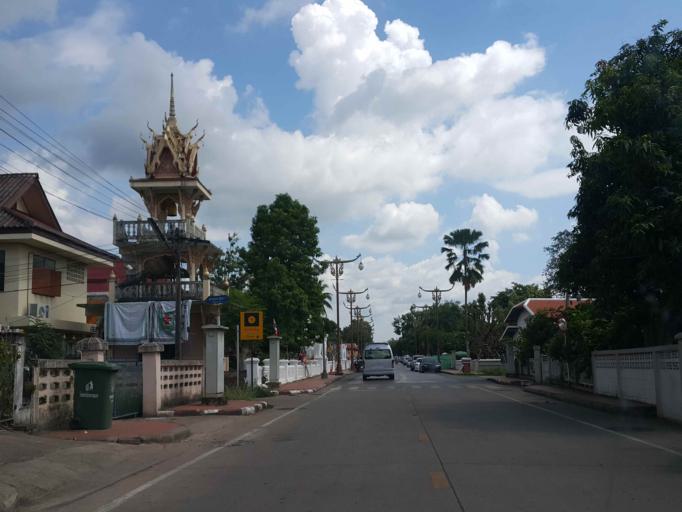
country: TH
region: Nan
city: Nan
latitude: 18.7734
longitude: 100.7720
